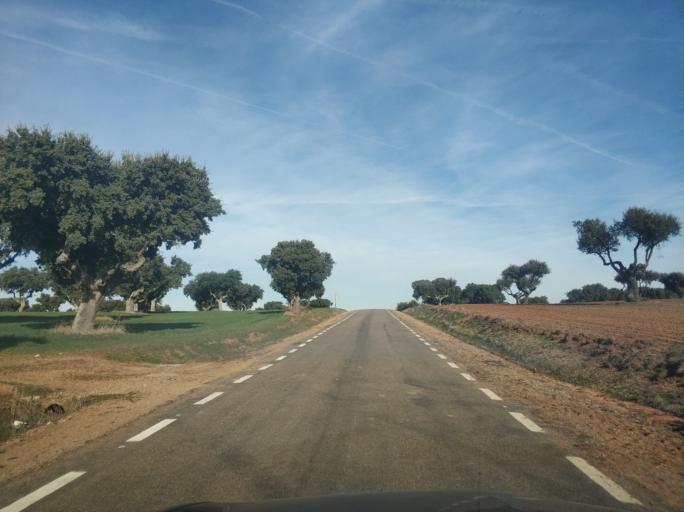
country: ES
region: Castille and Leon
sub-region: Provincia de Salamanca
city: Parada de Arriba
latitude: 40.9969
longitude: -5.8119
